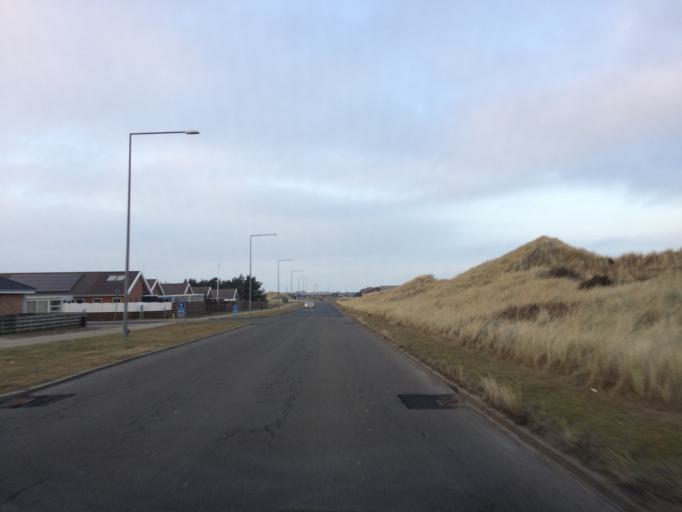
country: DK
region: Central Jutland
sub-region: Ringkobing-Skjern Kommune
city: Hvide Sande
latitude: 56.0246
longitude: 8.1174
